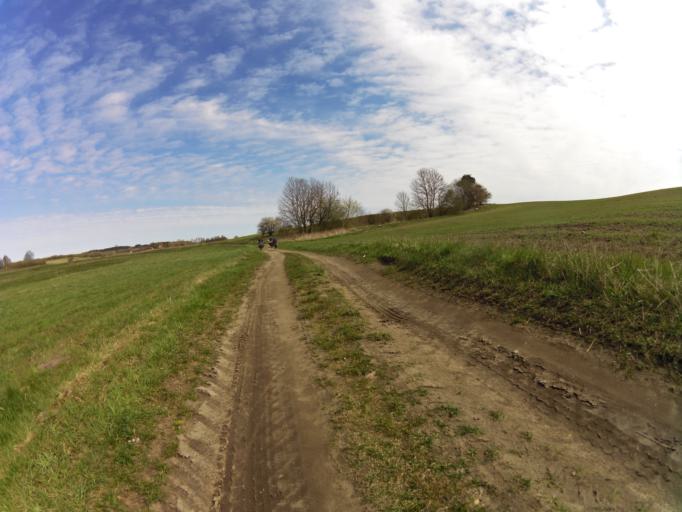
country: PL
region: West Pomeranian Voivodeship
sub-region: Powiat szczecinecki
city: Szczecinek
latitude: 53.7417
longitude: 16.5969
